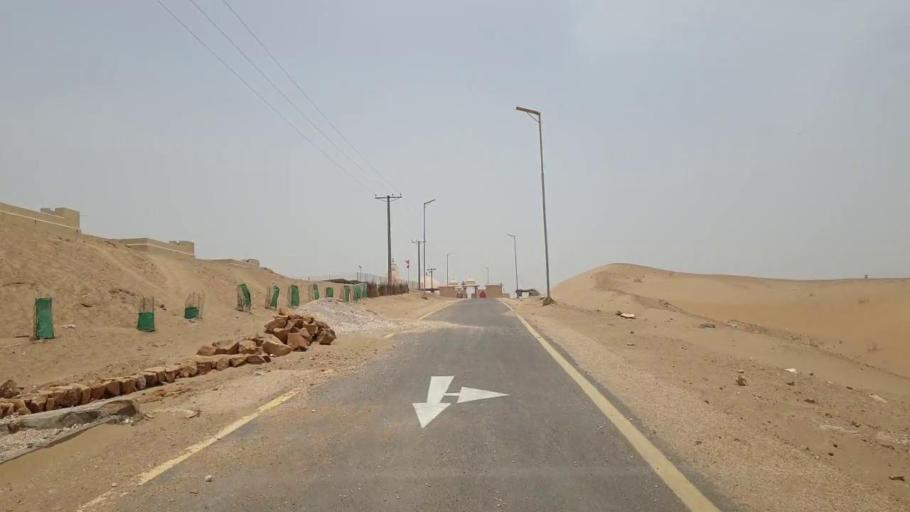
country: PK
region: Sindh
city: Islamkot
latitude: 24.7230
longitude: 70.3276
